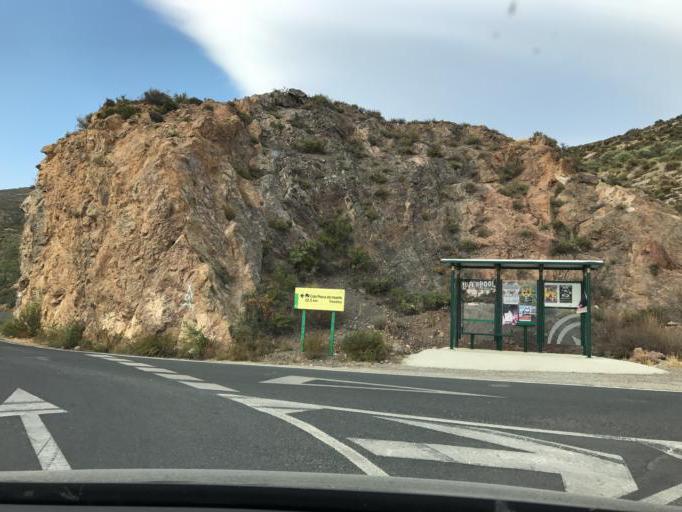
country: ES
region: Andalusia
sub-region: Provincia de Granada
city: Cadiar
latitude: 36.9618
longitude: -3.1766
